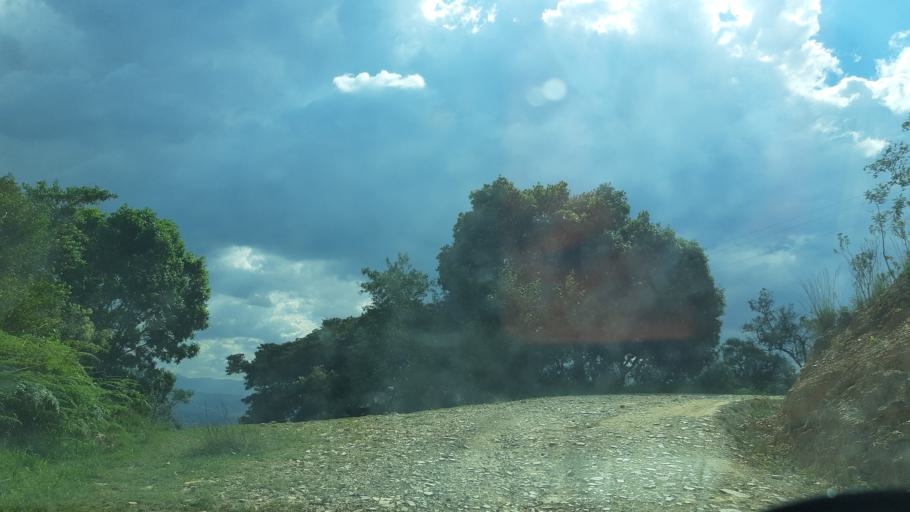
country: CO
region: Boyaca
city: Santa Sofia
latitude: 5.7263
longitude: -73.5488
